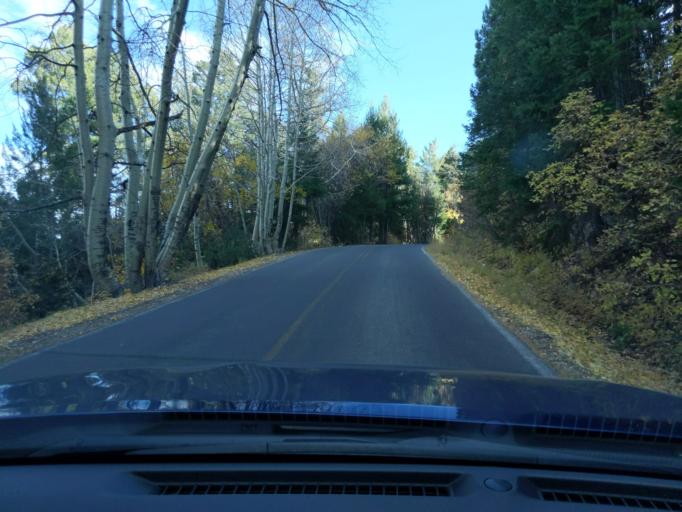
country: US
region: Arizona
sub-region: Pima County
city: Catalina
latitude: 32.4444
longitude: -110.7865
